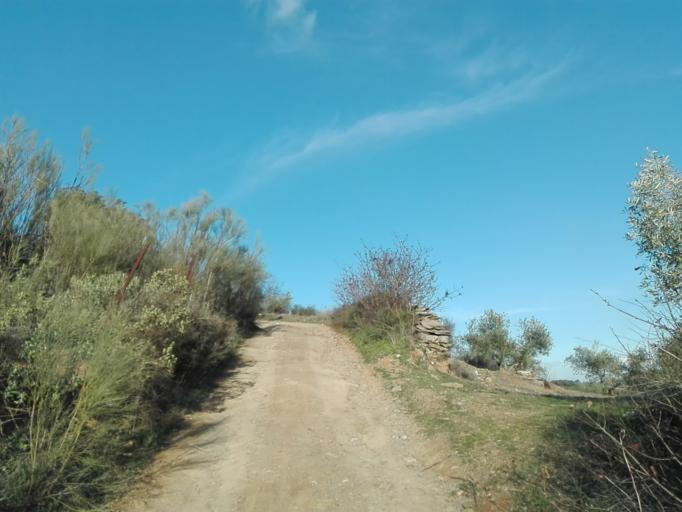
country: ES
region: Extremadura
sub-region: Provincia de Badajoz
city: Trasierra
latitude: 38.2043
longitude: -5.9997
